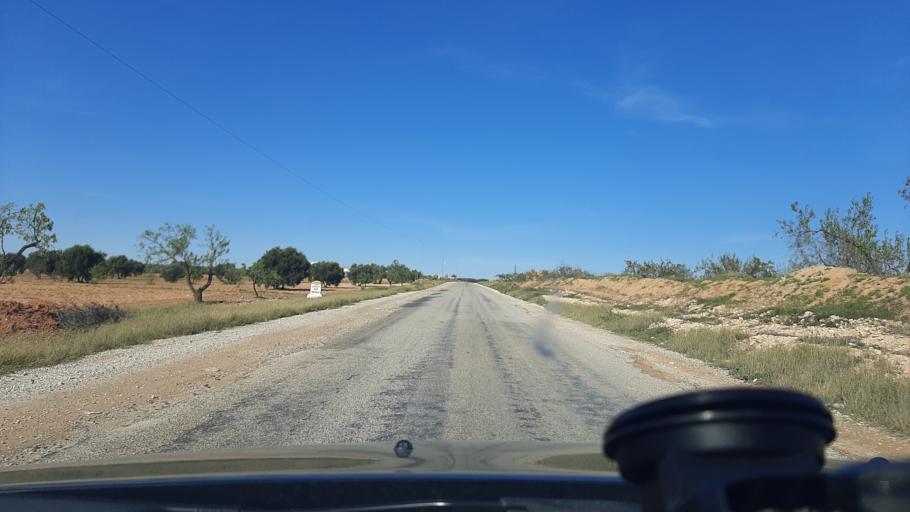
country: TN
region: Safaqis
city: Sfax
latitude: 34.9446
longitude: 10.5531
